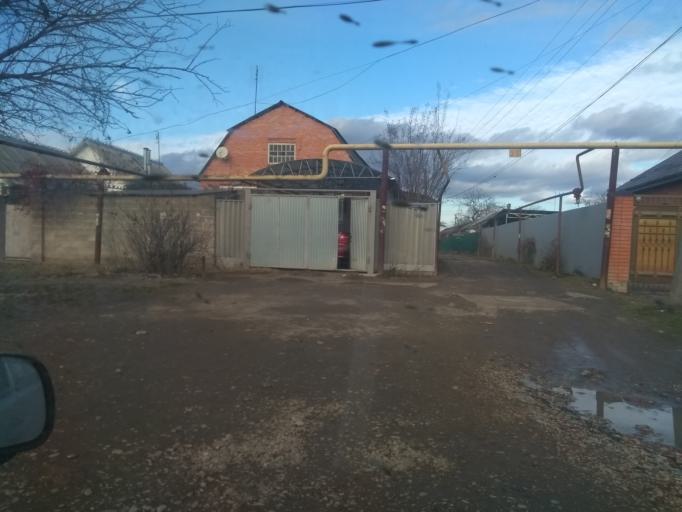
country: RU
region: Stavropol'skiy
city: Krasnokumskoye
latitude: 44.1764
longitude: 43.4814
